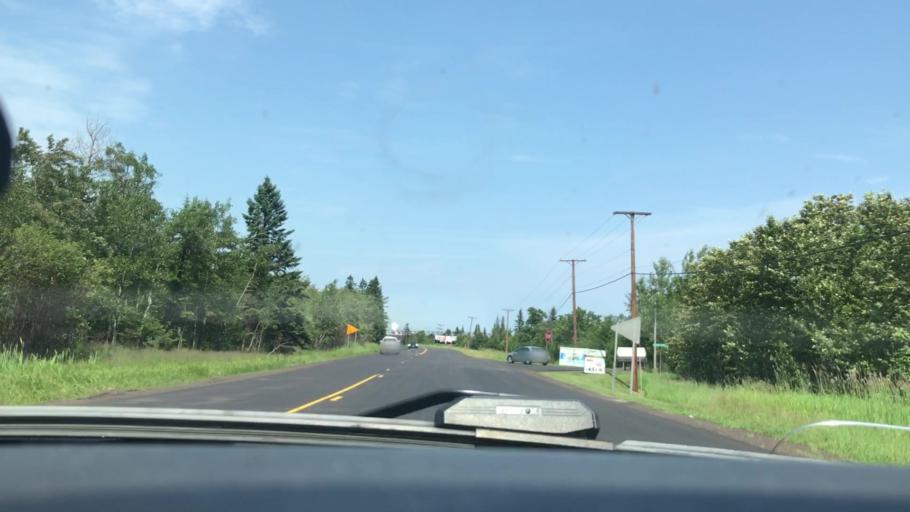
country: US
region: Minnesota
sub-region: Lake County
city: Silver Bay
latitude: 47.2719
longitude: -91.2787
